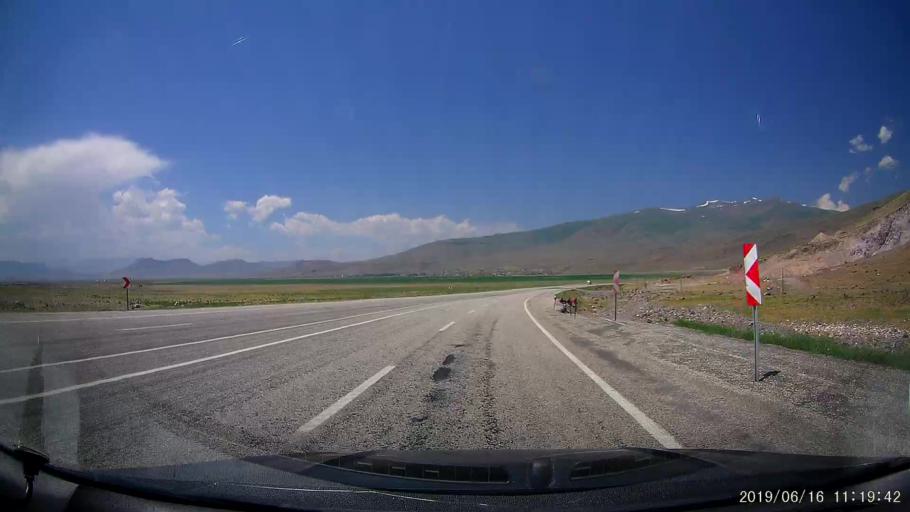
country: TR
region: Agri
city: Dogubayazit
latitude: 39.6963
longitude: 44.1088
